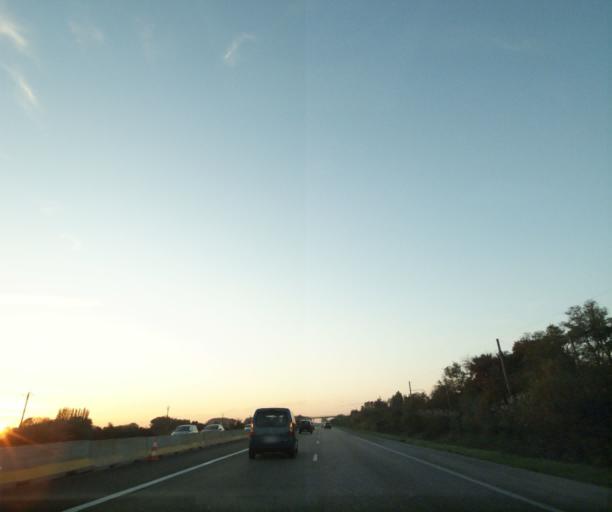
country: FR
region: Provence-Alpes-Cote d'Azur
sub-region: Departement des Bouches-du-Rhone
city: Arles
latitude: 43.6455
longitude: 4.6968
